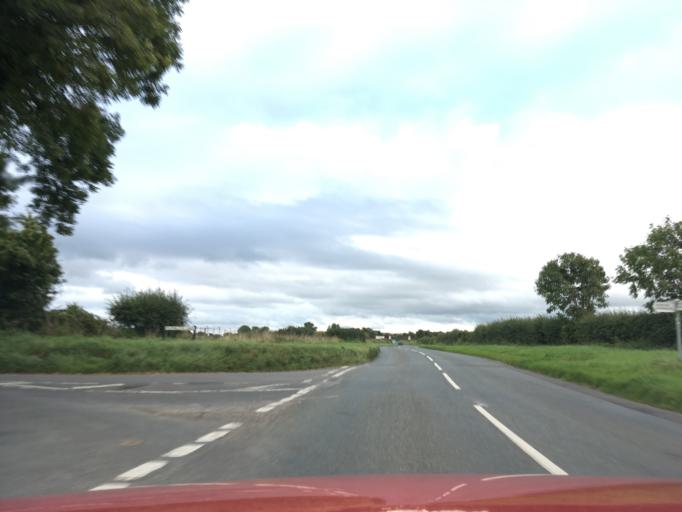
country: GB
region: England
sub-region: South Gloucestershire
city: Alveston
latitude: 51.5936
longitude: -2.5488
